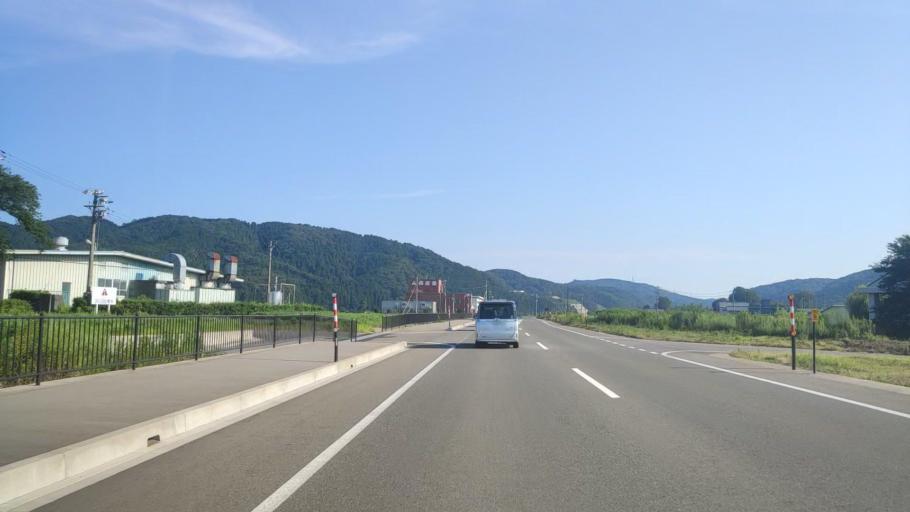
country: JP
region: Fukui
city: Maruoka
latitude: 36.1964
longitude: 136.2674
